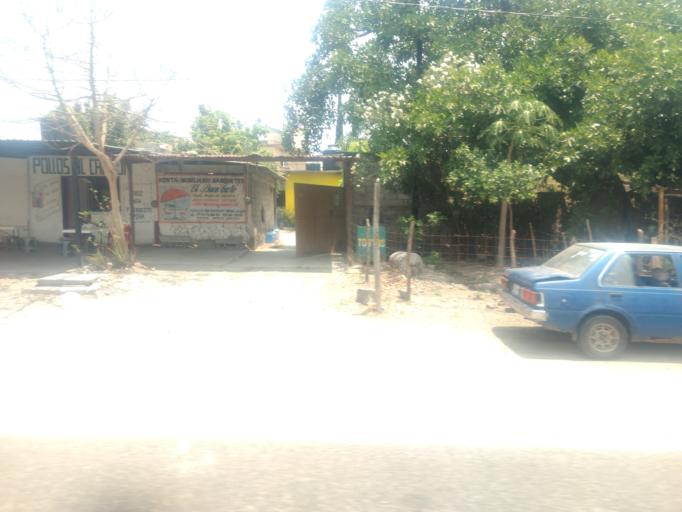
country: MX
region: Morelos
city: La Joya
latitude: 18.7024
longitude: -99.4791
